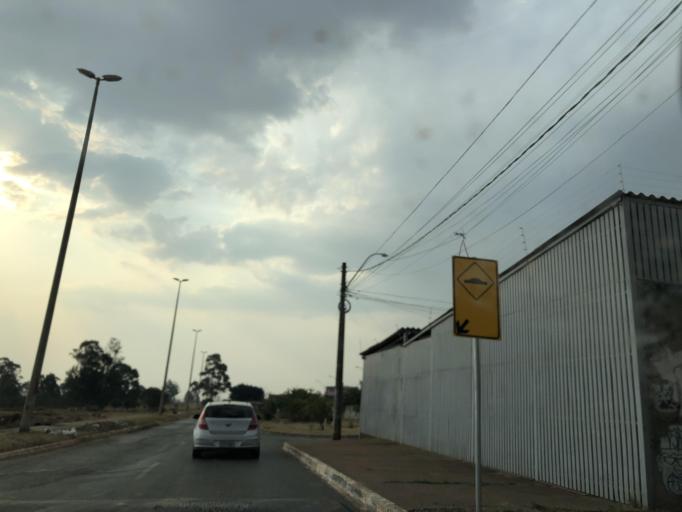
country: BR
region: Federal District
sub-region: Brasilia
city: Brasilia
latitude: -15.9244
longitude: -48.0567
